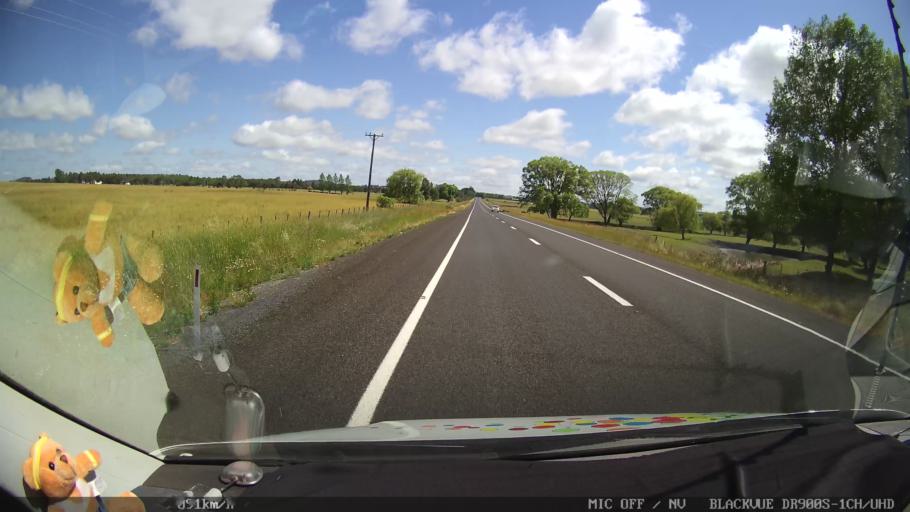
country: AU
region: New South Wales
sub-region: Glen Innes Severn
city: Glen Innes
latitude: -29.8316
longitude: 151.7377
